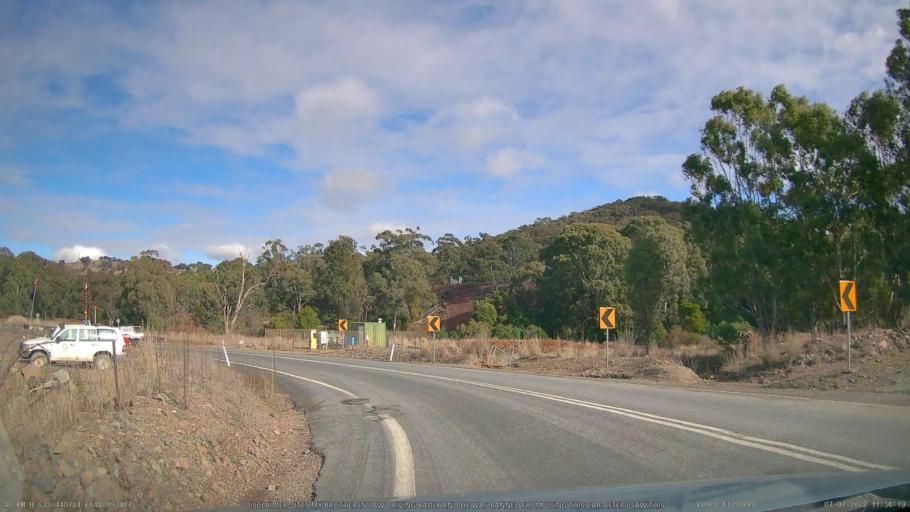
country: AU
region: New South Wales
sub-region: Orange Municipality
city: Orange
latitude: -33.4408
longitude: 148.9972
